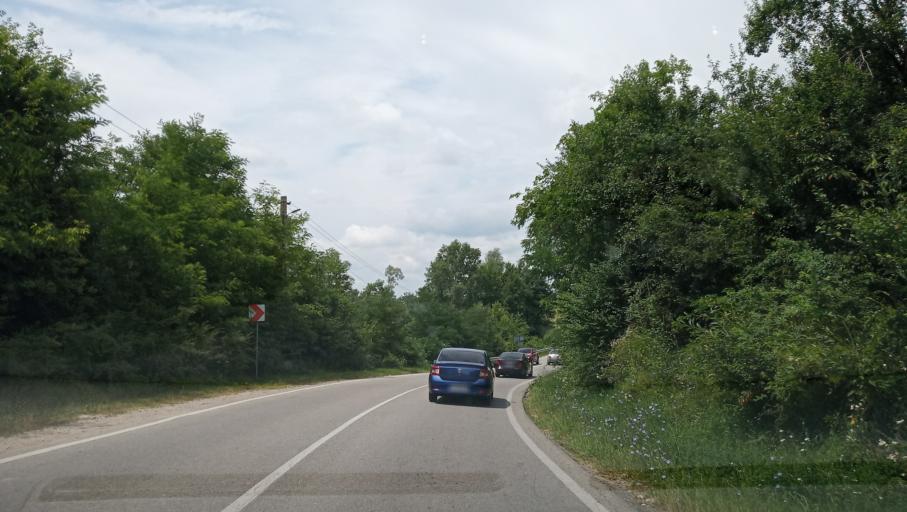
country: RO
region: Gorj
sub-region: Comuna Lelesti
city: Lelesti
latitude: 45.0819
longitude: 23.1720
